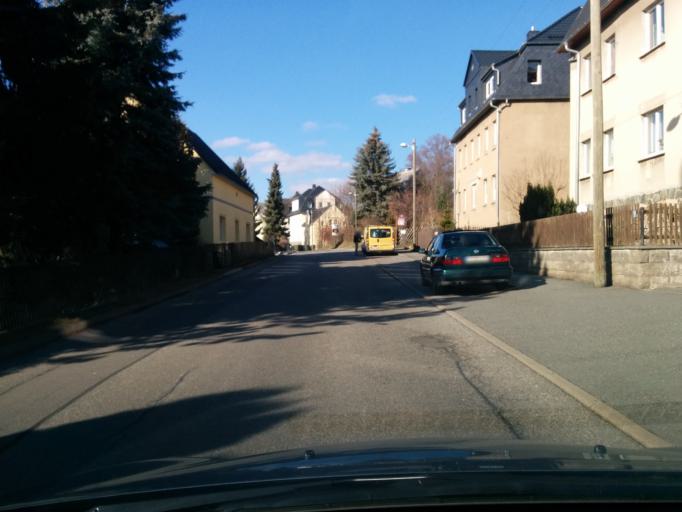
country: DE
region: Saxony
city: Neukirchen
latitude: 50.7826
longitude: 12.8546
